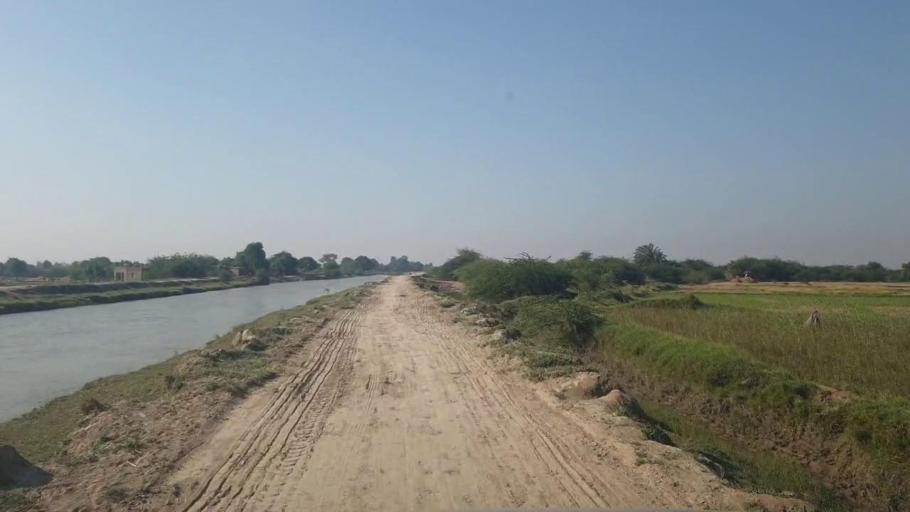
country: PK
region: Sindh
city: Badin
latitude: 24.6834
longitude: 68.8602
